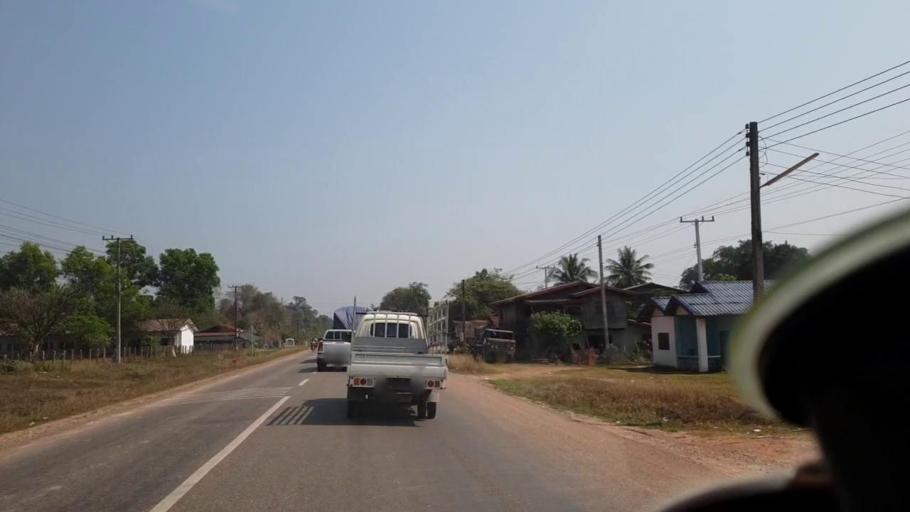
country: TH
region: Nong Khai
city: Phon Phisai
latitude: 18.1293
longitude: 103.0376
